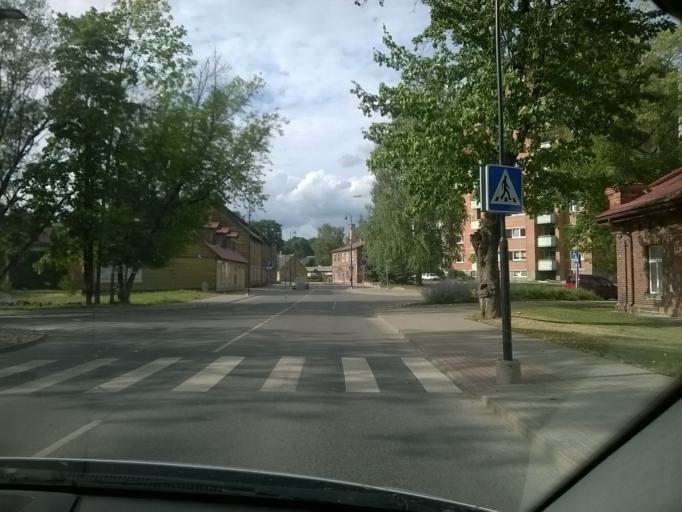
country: EE
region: Vorumaa
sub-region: Voru linn
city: Voru
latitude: 57.8403
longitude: 27.0023
